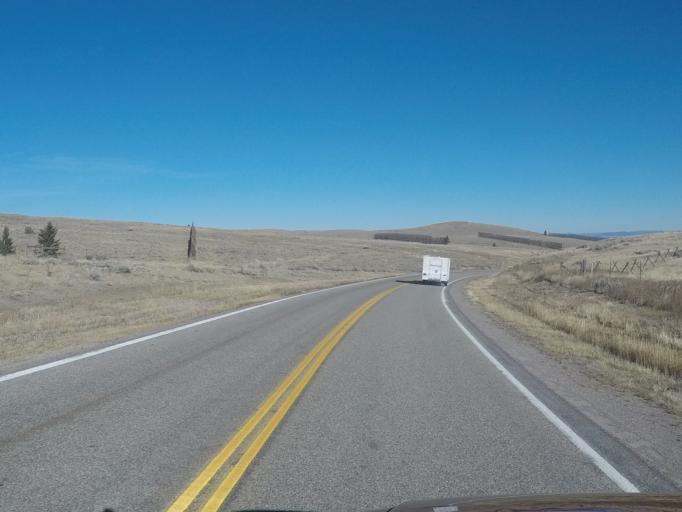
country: US
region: Montana
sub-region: Meagher County
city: White Sulphur Springs
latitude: 46.3852
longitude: -110.9908
